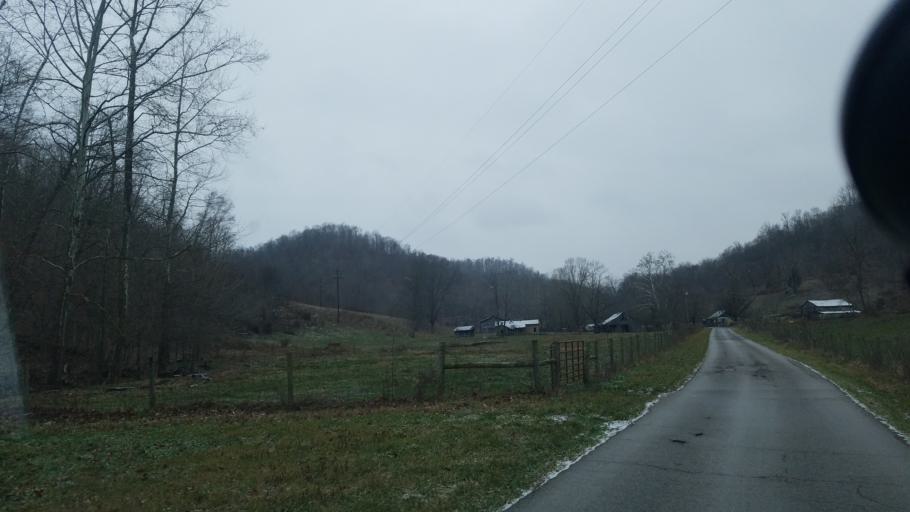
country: US
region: Kentucky
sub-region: Lewis County
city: Vanceburg
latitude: 38.4816
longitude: -83.4962
